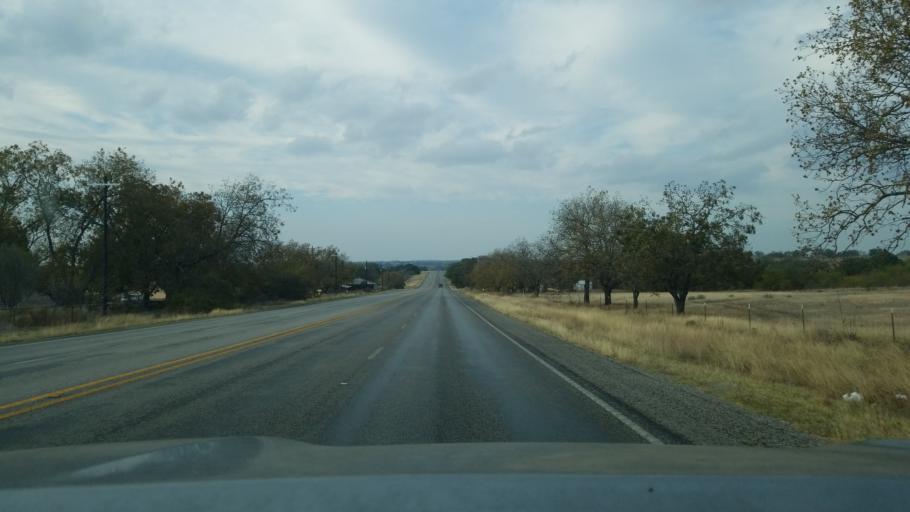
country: US
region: Texas
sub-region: Mills County
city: Goldthwaite
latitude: 31.4922
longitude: -98.5754
